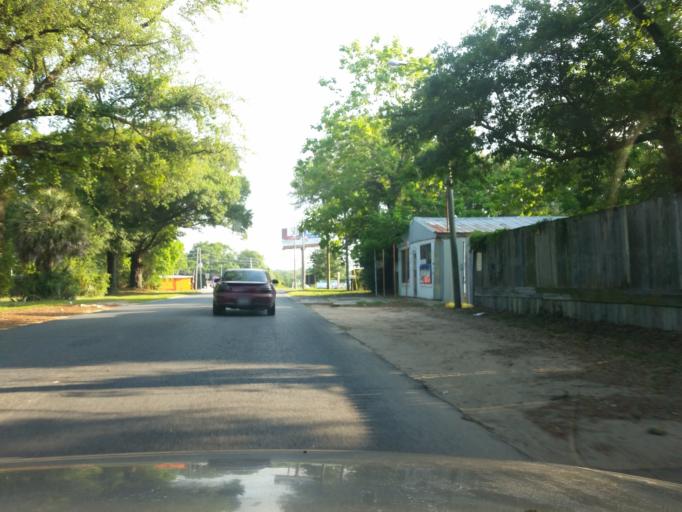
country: US
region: Florida
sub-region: Escambia County
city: West Pensacola
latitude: 30.4371
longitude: -87.2604
